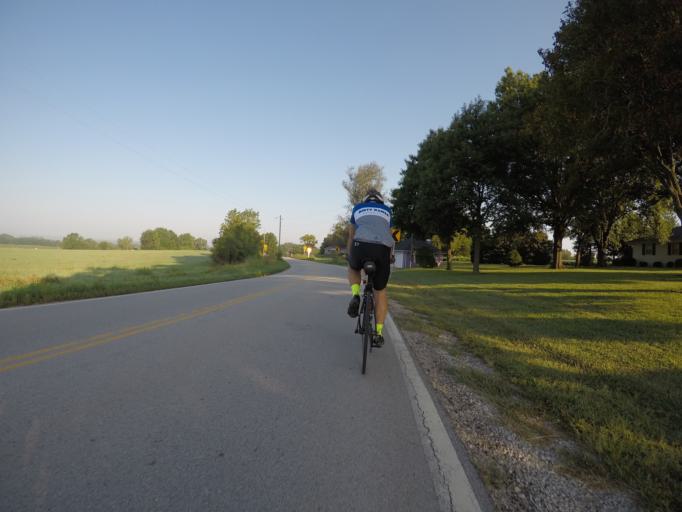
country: US
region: Kansas
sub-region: Leavenworth County
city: Lansing
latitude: 39.2405
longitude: -94.8686
